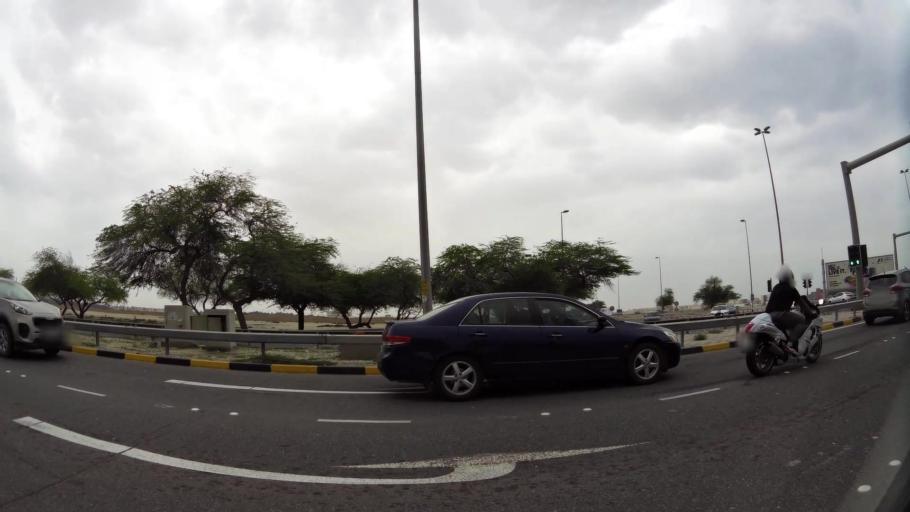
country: BH
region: Central Governorate
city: Dar Kulayb
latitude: 26.0569
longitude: 50.4999
